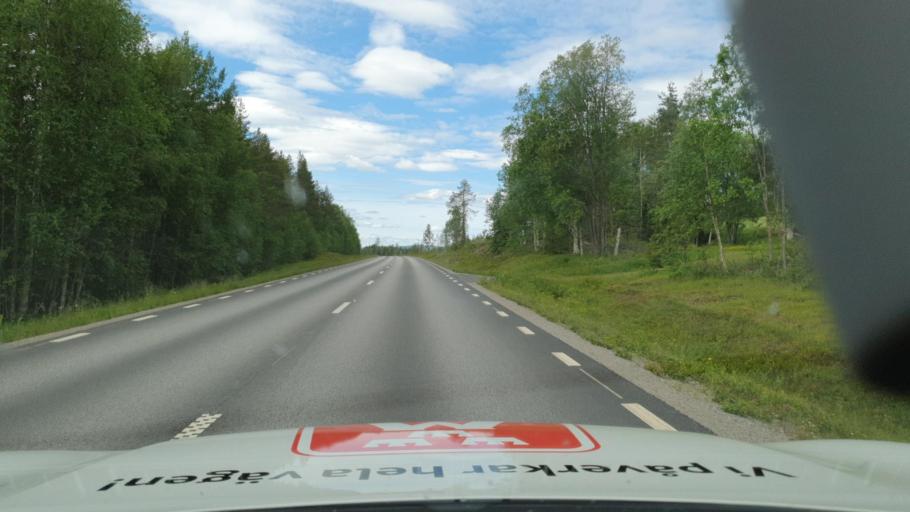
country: SE
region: Vaesterbotten
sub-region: Norsjo Kommun
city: Norsjoe
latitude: 65.2135
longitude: 19.7831
